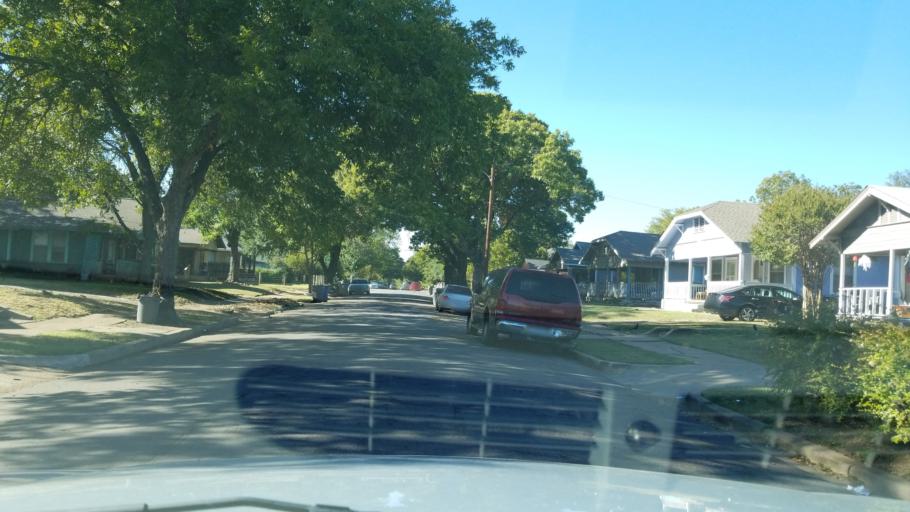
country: US
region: Texas
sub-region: Dallas County
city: Highland Park
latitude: 32.7989
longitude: -96.7438
